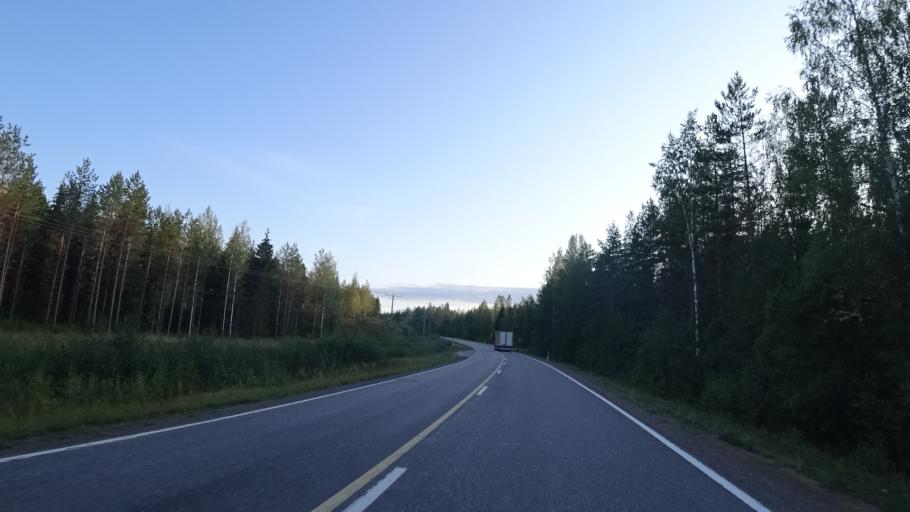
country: FI
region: South Karelia
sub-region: Lappeenranta
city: Ylaemaa
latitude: 60.7884
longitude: 28.0006
